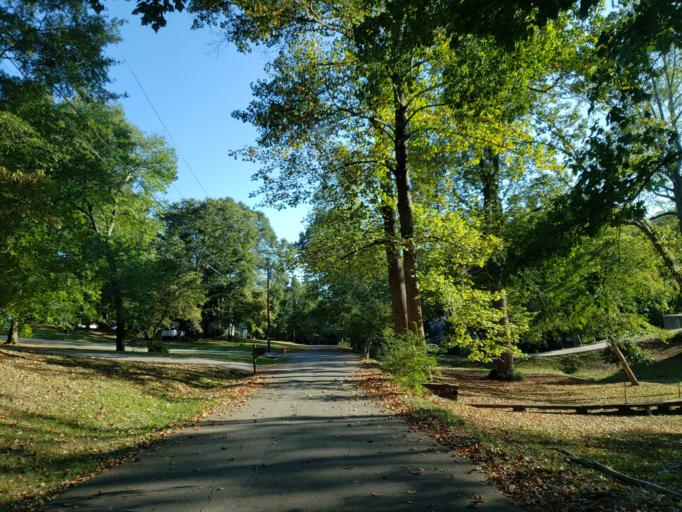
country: US
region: Georgia
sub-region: Cherokee County
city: Ball Ground
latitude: 34.3377
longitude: -84.3845
